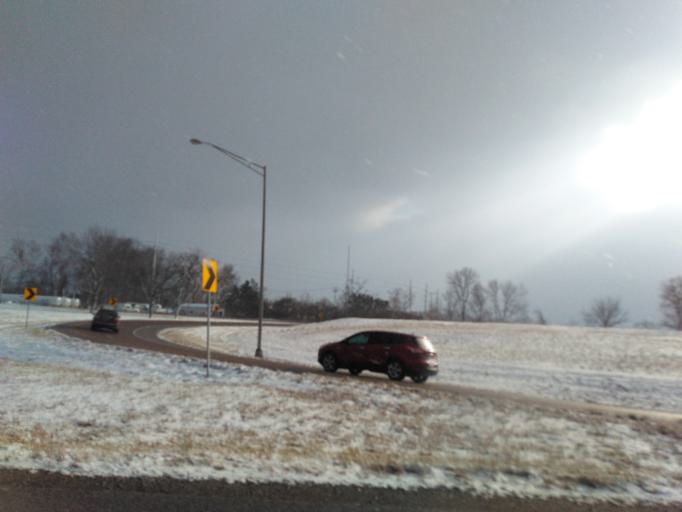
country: US
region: Illinois
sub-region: Madison County
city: Maryville
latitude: 38.7082
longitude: -89.9577
